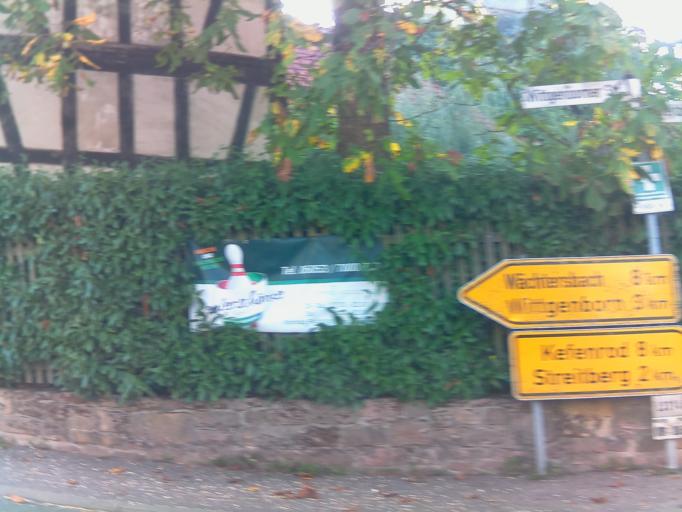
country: DE
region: Hesse
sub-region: Regierungsbezirk Darmstadt
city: Birstein
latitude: 50.3079
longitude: 9.2688
